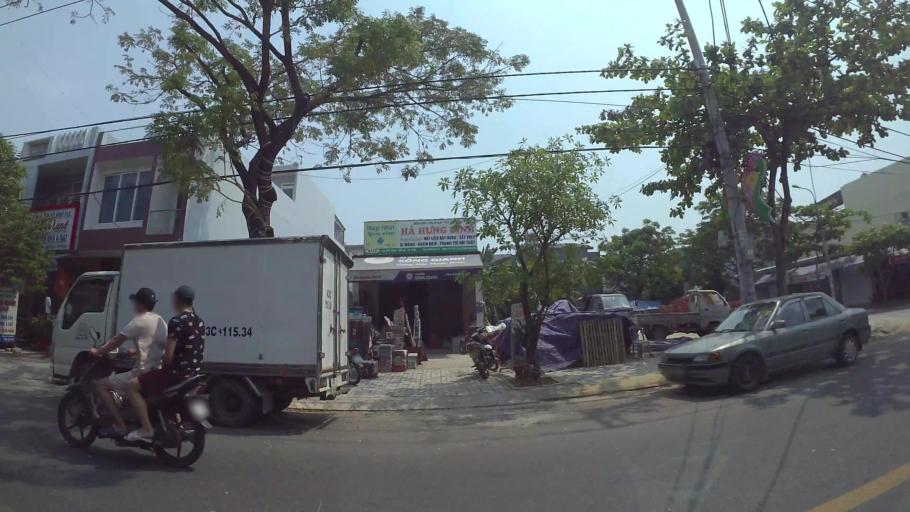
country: VN
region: Da Nang
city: Cam Le
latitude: 16.0009
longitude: 108.2131
